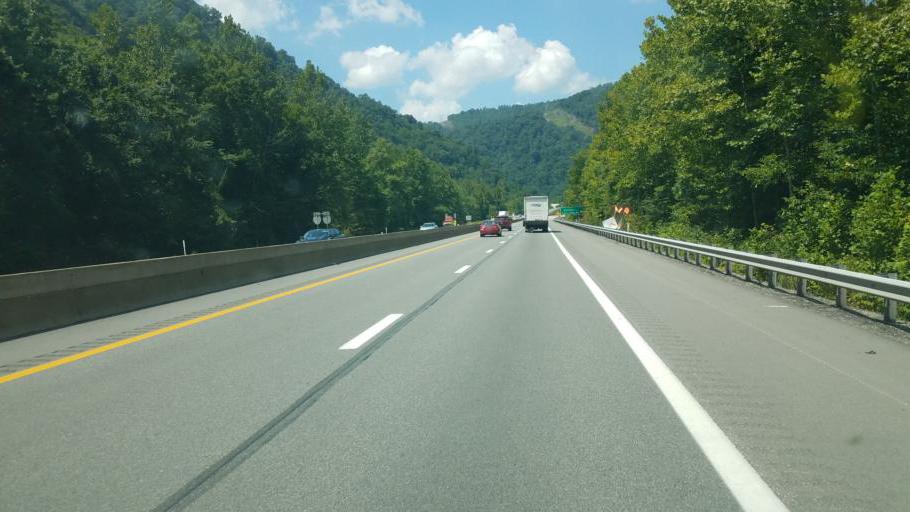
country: US
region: West Virginia
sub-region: Kanawha County
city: Montgomery
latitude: 38.1222
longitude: -81.3872
